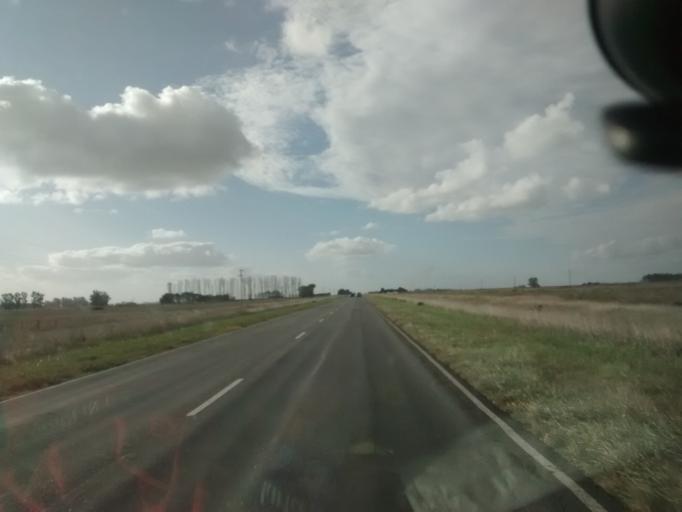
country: AR
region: Buenos Aires
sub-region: Partido de Ayacucho
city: Ayacucho
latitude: -36.9016
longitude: -58.5299
